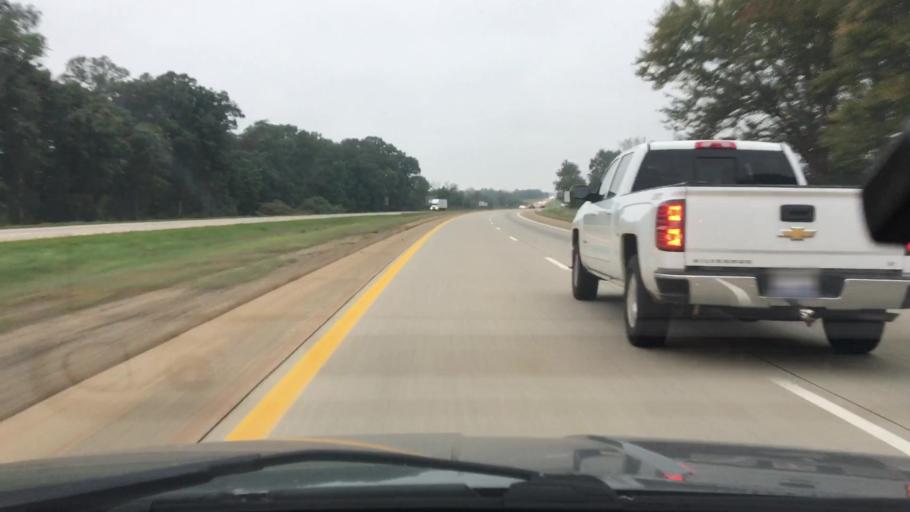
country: US
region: Michigan
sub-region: Jackson County
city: Concord
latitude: 42.2625
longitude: -84.6313
